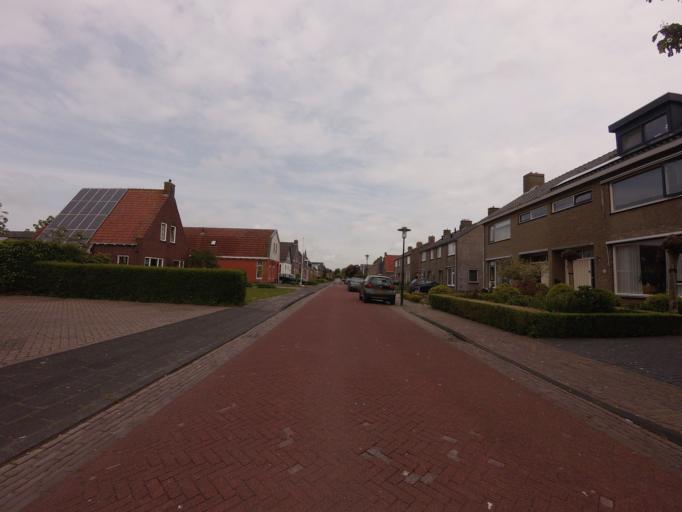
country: NL
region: Friesland
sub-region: Sudwest Fryslan
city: Bolsward
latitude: 53.0809
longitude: 5.4823
